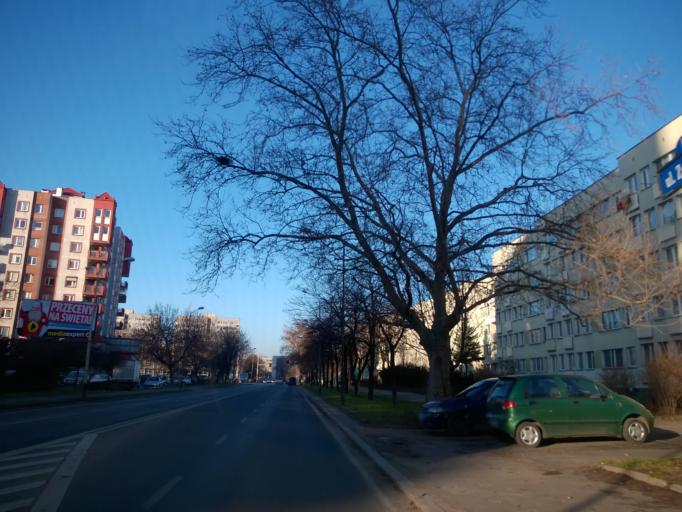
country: PL
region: Lower Silesian Voivodeship
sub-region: Powiat wroclawski
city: Wroclaw
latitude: 51.1169
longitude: 17.0094
